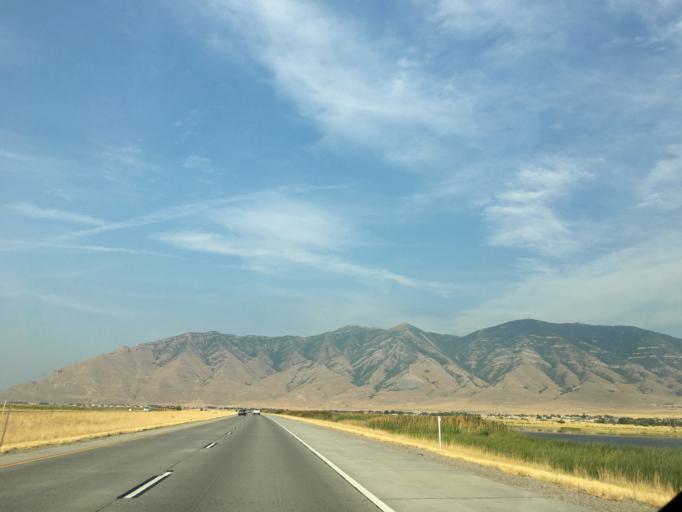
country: US
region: Utah
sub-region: Tooele County
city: Stansbury park
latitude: 40.6658
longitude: -112.3107
